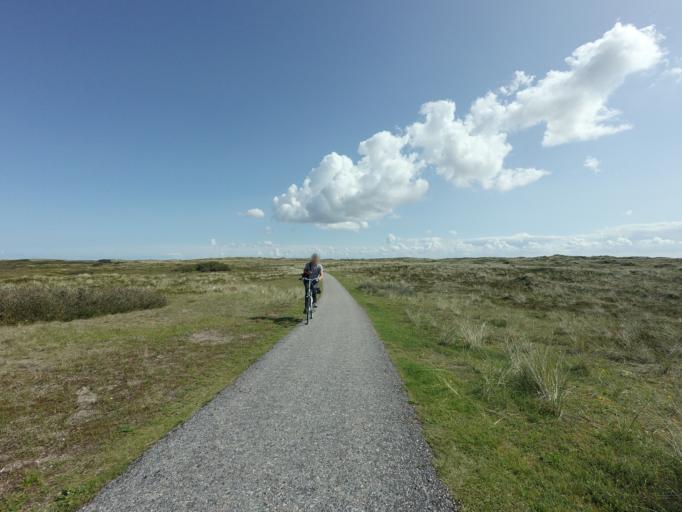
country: NL
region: Friesland
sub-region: Gemeente Terschelling
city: West-Terschelling
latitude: 53.4126
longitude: 5.3736
